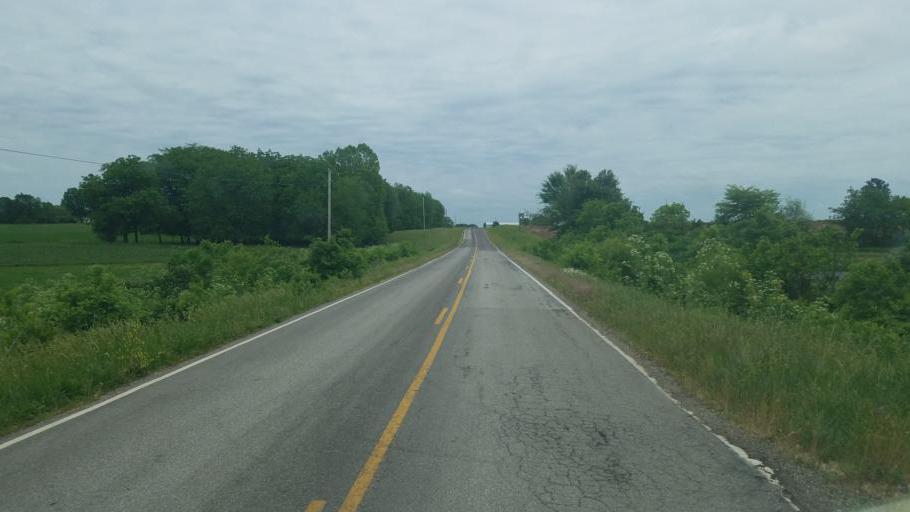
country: US
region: Missouri
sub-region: Morgan County
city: Versailles
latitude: 38.5107
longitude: -92.7541
